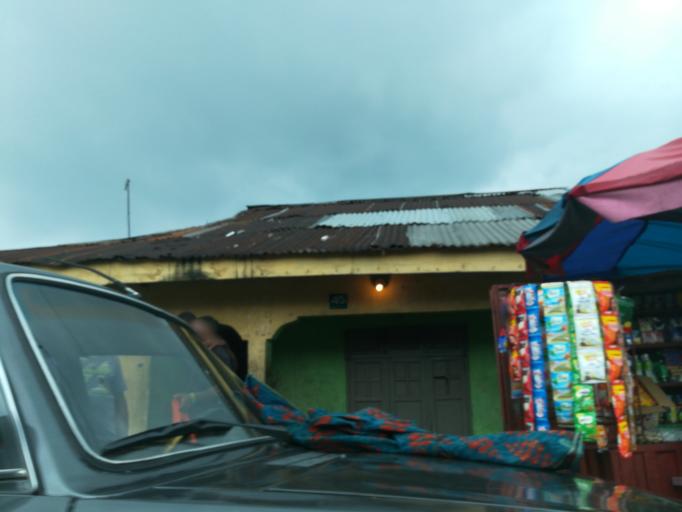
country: NG
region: Rivers
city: Port Harcourt
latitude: 4.7967
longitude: 6.9902
